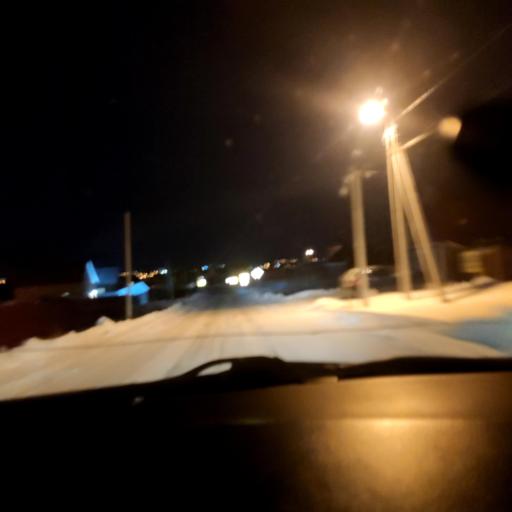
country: RU
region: Bashkortostan
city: Kabakovo
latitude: 54.6680
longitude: 56.2181
